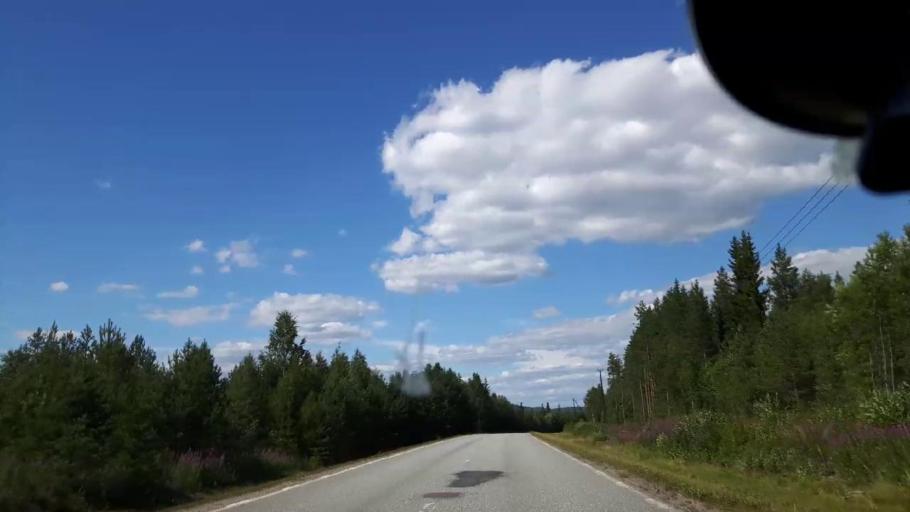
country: SE
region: Vaesternorrland
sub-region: Ange Kommun
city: Fransta
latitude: 62.7175
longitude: 16.3336
